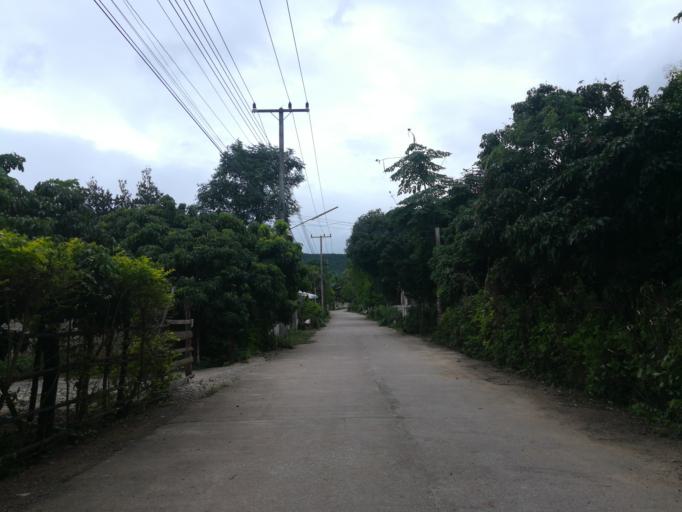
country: TH
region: Chiang Mai
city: Chom Thong
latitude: 18.4048
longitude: 98.6505
